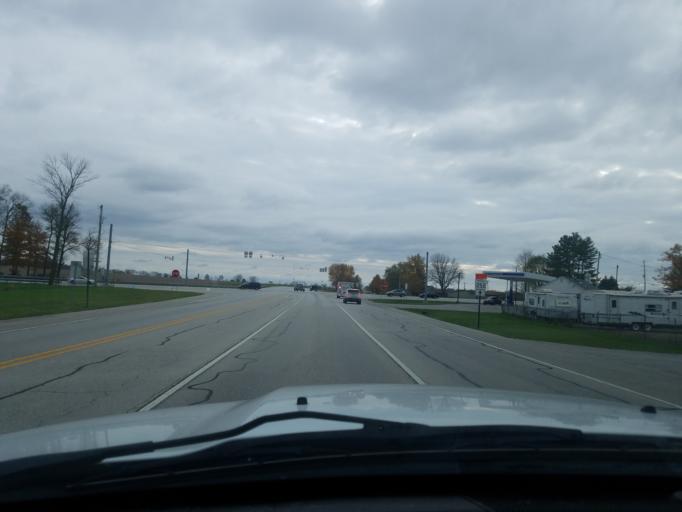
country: US
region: Indiana
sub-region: Bartholomew County
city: Hope
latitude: 39.2261
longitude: -85.7719
